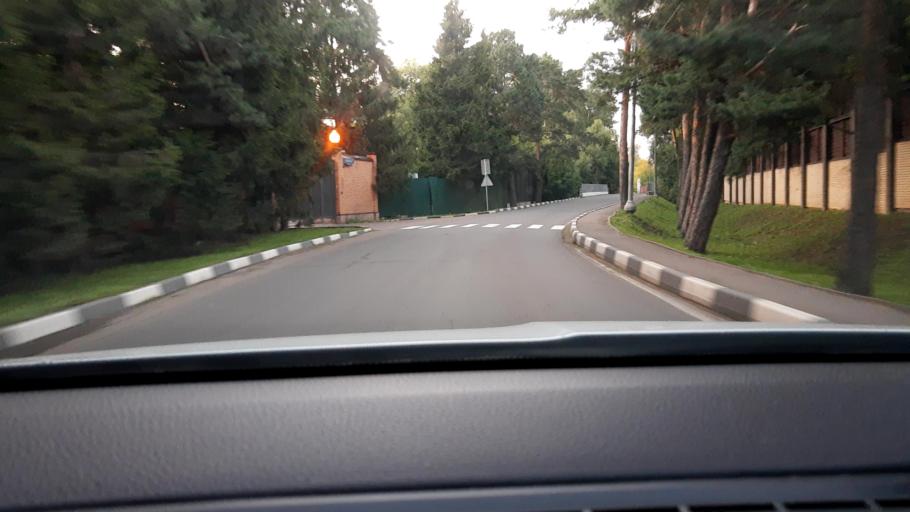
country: RU
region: Moskovskaya
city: Zarech'ye
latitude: 55.6905
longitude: 37.3829
